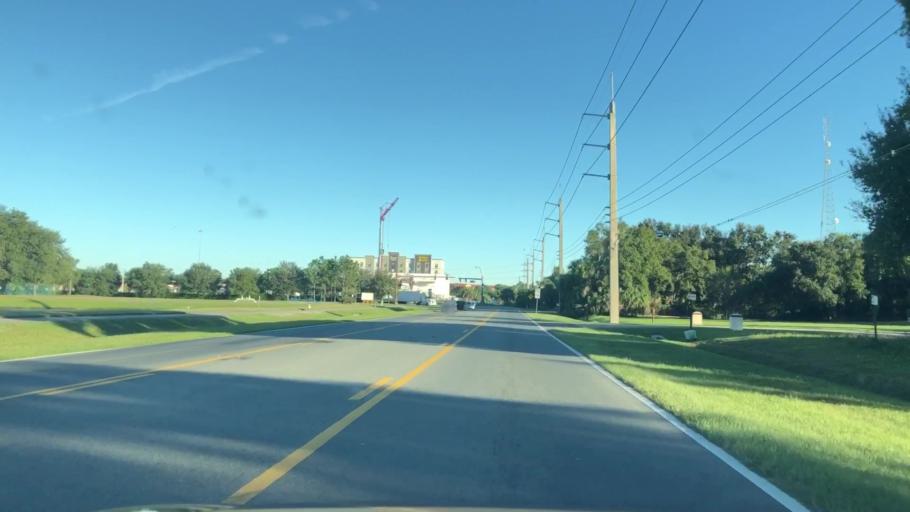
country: US
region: Florida
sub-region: Sarasota County
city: Fruitville
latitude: 27.3338
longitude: -82.4493
